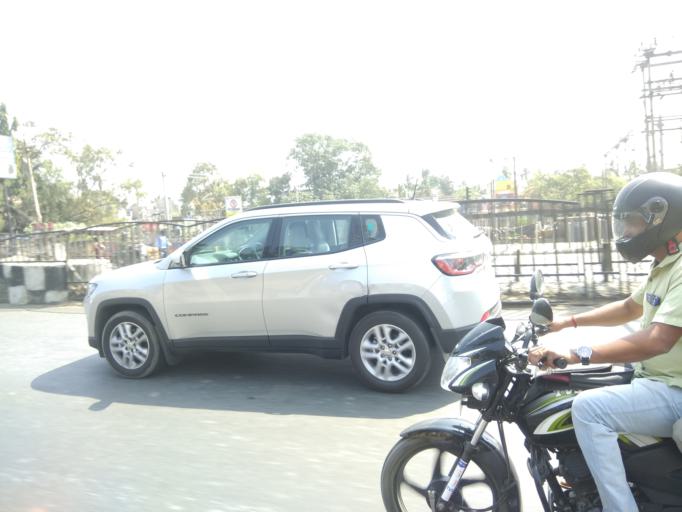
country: IN
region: Tamil Nadu
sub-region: Kancheepuram
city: Pallavaram
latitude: 12.9528
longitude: 80.1412
